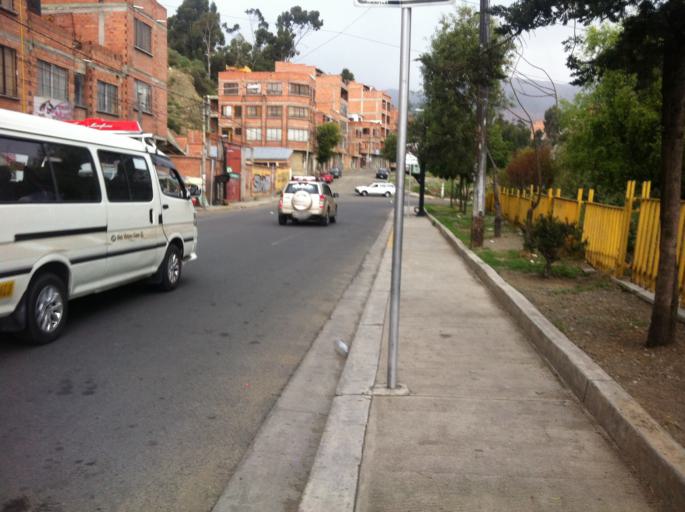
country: BO
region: La Paz
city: La Paz
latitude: -16.4919
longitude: -68.1195
